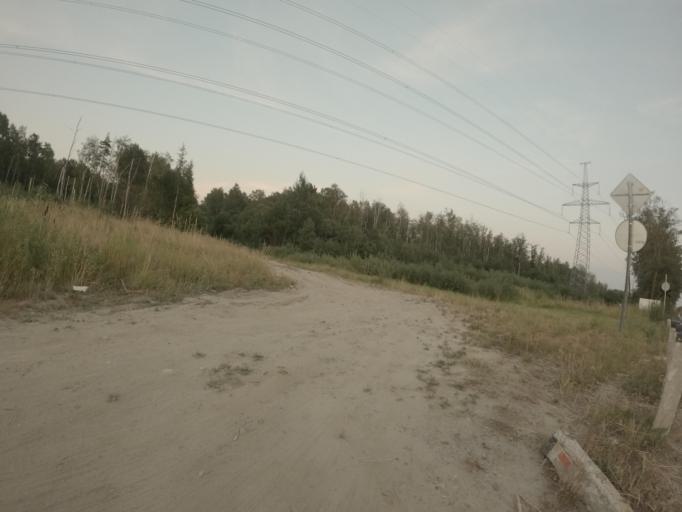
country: RU
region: St.-Petersburg
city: Krasnogvargeisky
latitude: 59.9436
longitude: 30.5216
